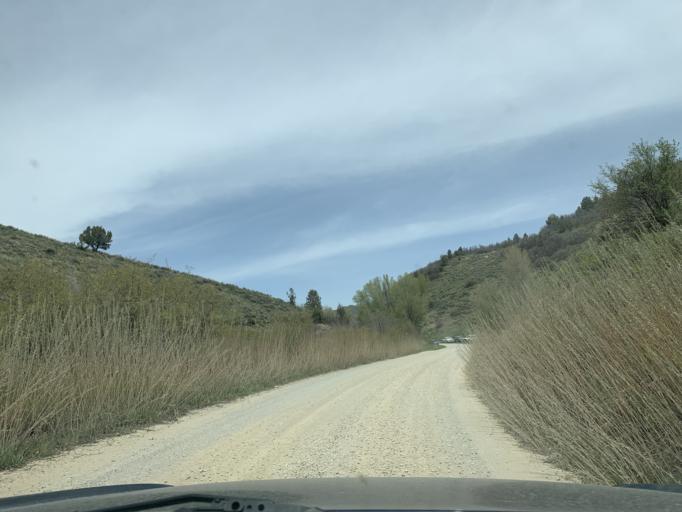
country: US
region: Utah
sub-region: Utah County
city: Mapleton
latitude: 40.1684
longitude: -111.3306
